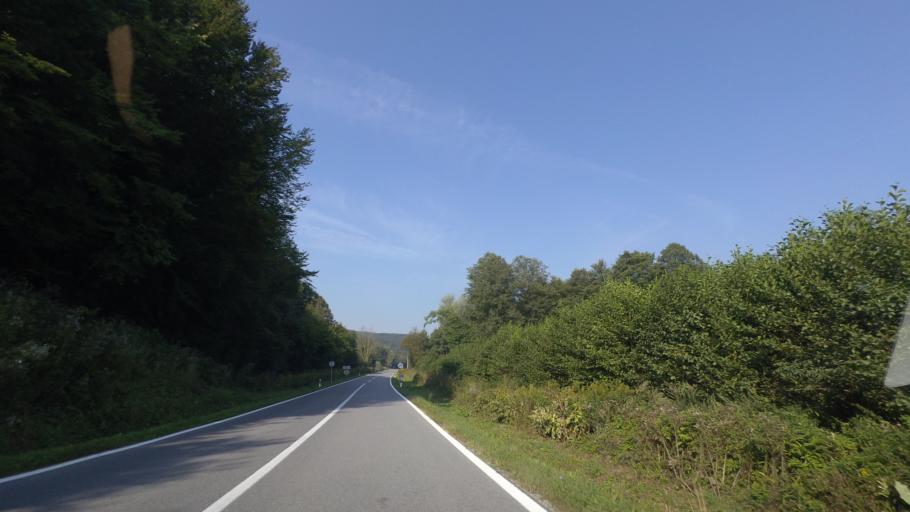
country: HR
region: Bjelovarsko-Bilogorska
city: Sirac
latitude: 45.4683
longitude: 17.3508
